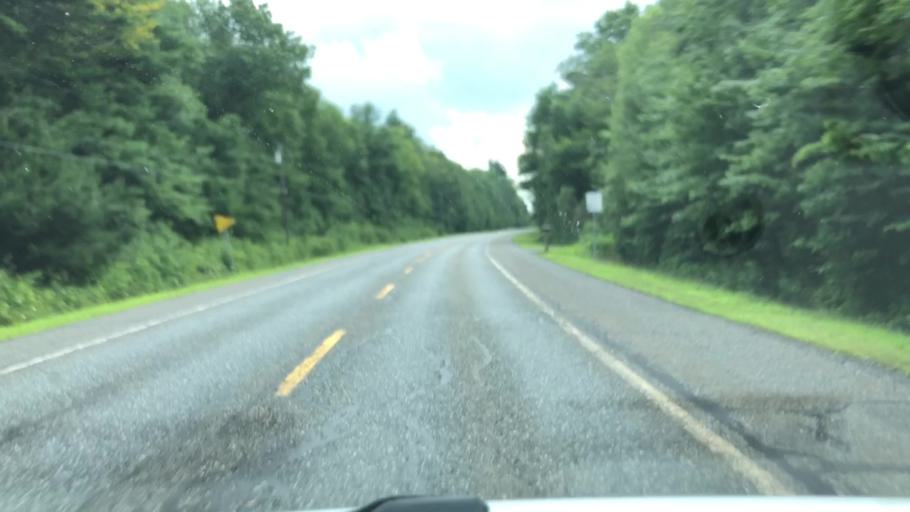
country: US
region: Massachusetts
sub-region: Franklin County
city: Ashfield
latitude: 42.4644
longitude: -72.8063
